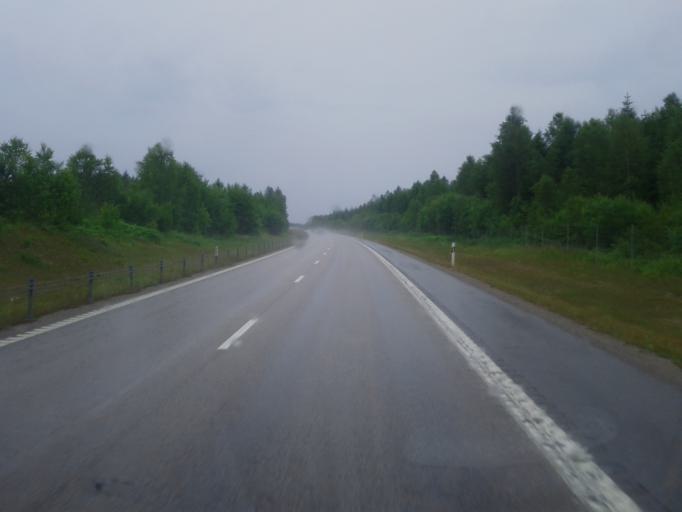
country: SE
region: Uppsala
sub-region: Tierps Kommun
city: Tierp
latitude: 60.3808
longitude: 17.4817
